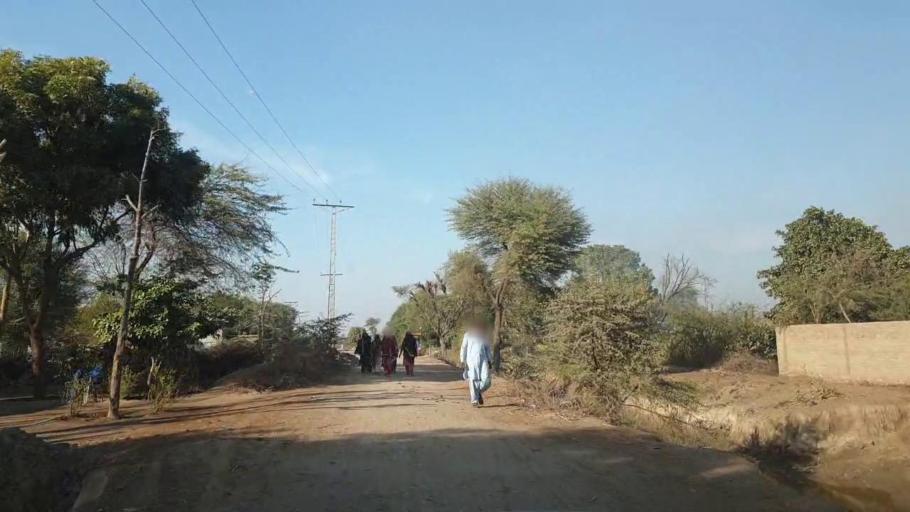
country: PK
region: Sindh
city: Tando Adam
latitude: 25.7104
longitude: 68.7042
